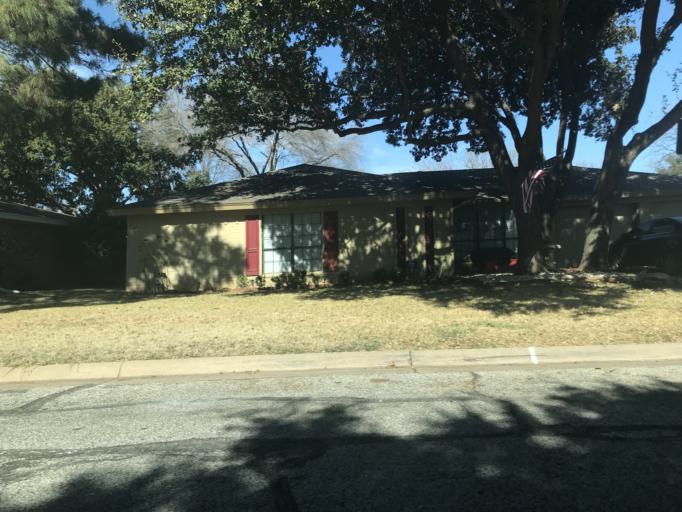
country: US
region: Texas
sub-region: Tom Green County
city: San Angelo
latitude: 31.4285
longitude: -100.4931
